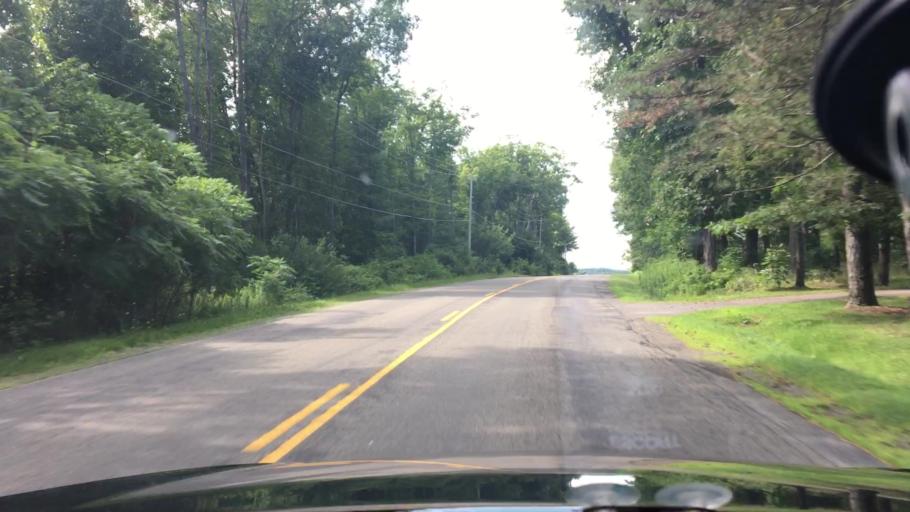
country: US
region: New York
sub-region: Chautauqua County
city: Lakewood
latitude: 42.1056
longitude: -79.3822
